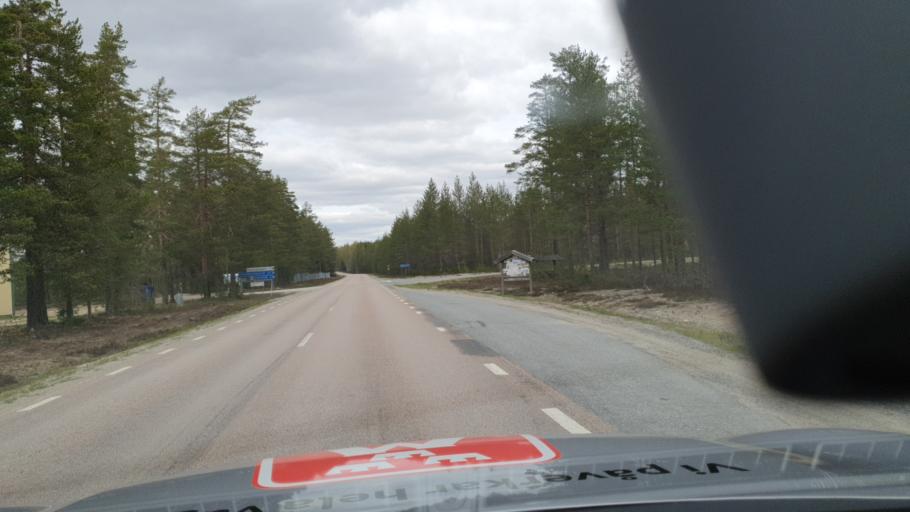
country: SE
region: Vaesternorrland
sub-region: OErnskoeldsviks Kommun
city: Husum
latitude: 63.4578
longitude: 18.9569
